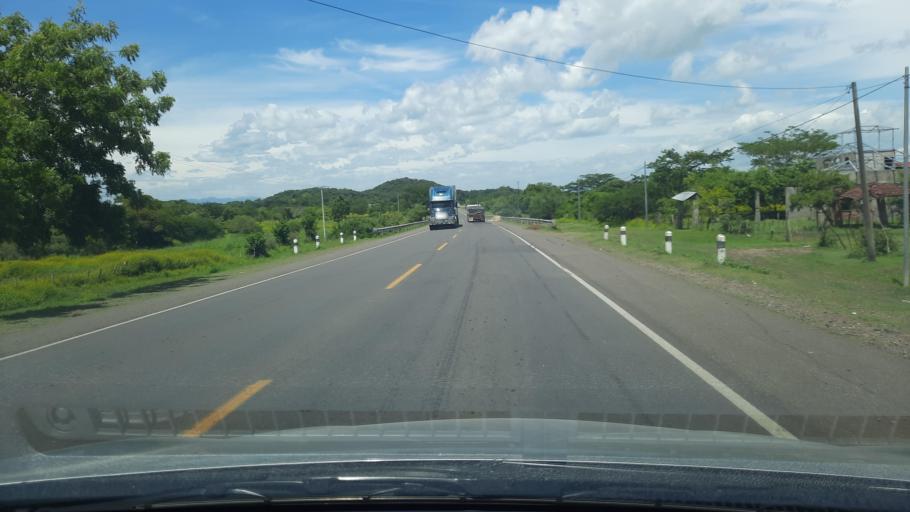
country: NI
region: Chinandega
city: Somotillo
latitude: 13.0556
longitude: -86.9205
